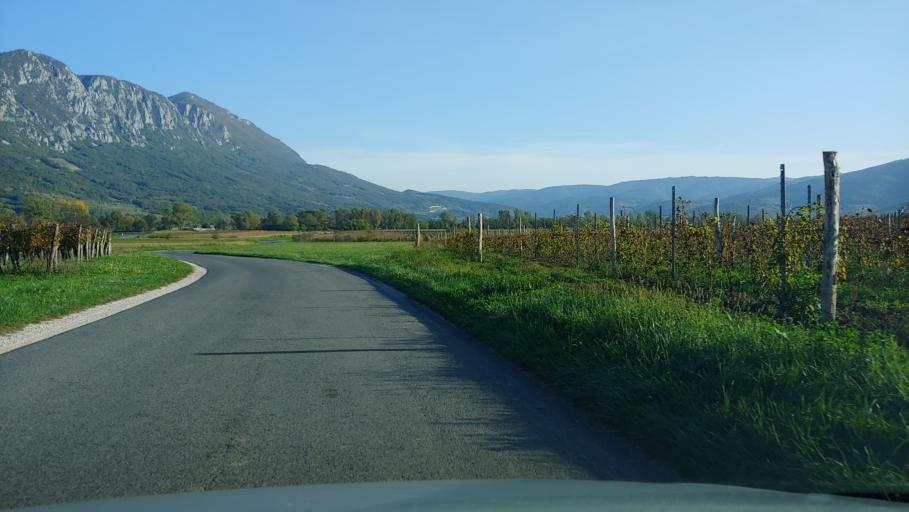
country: SI
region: Vipava
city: Vipava
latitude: 45.8396
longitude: 13.9427
